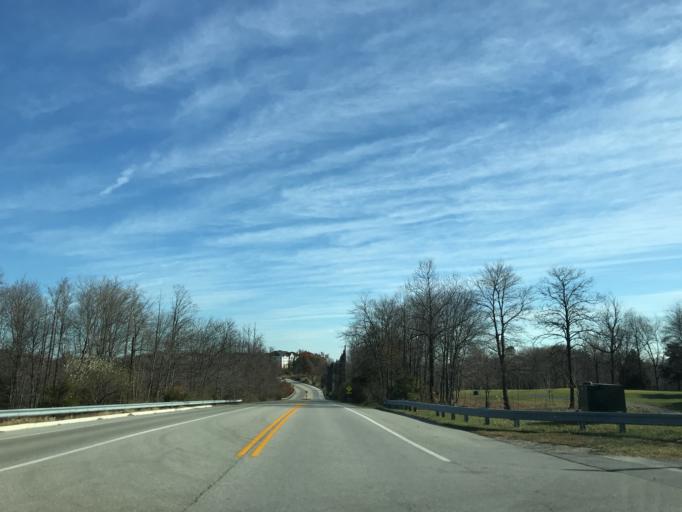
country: US
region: Maryland
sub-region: Howard County
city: West Elkridge
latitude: 39.2041
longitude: -76.7716
